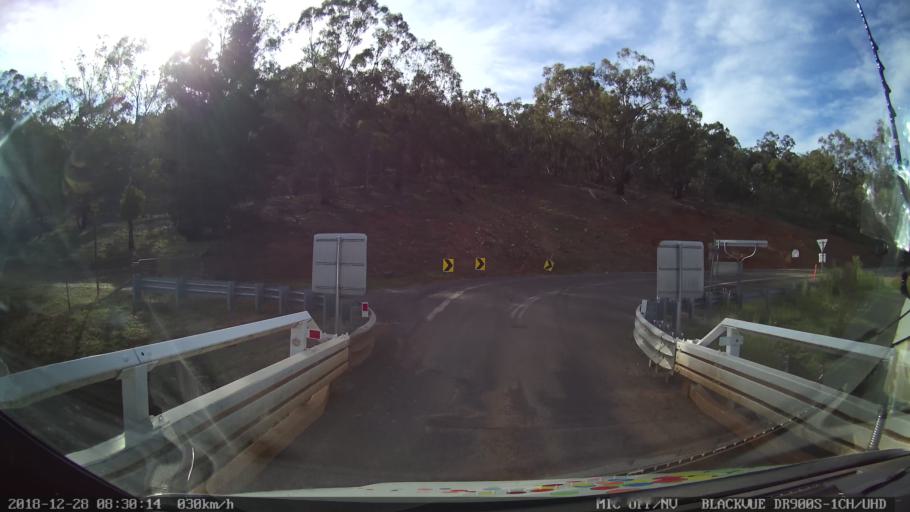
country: AU
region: New South Wales
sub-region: Blayney
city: Blayney
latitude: -33.9551
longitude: 149.3252
